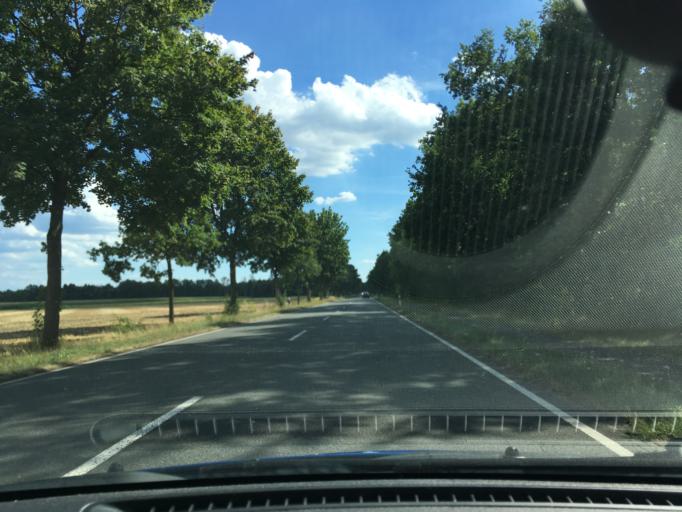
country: DE
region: Lower Saxony
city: Munster
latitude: 52.9461
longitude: 10.1304
